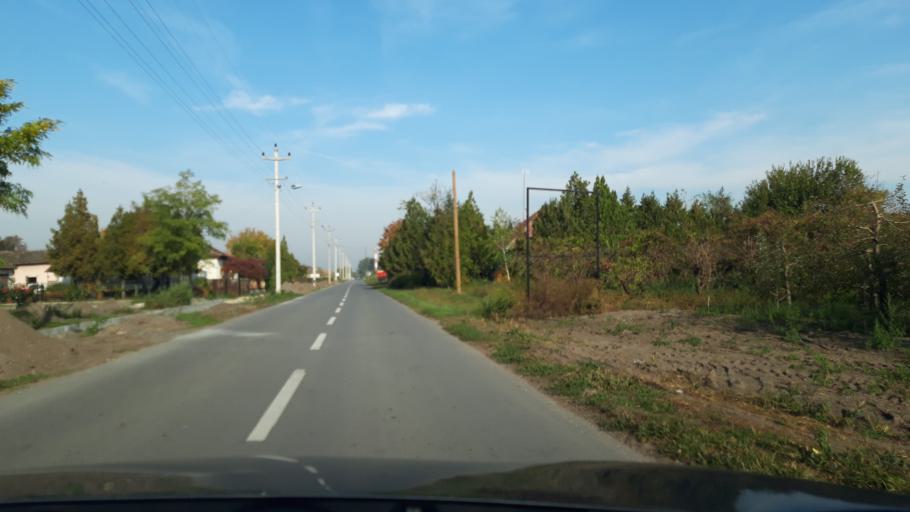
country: HU
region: Csongrad
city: Morahalom
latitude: 46.1370
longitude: 19.8502
